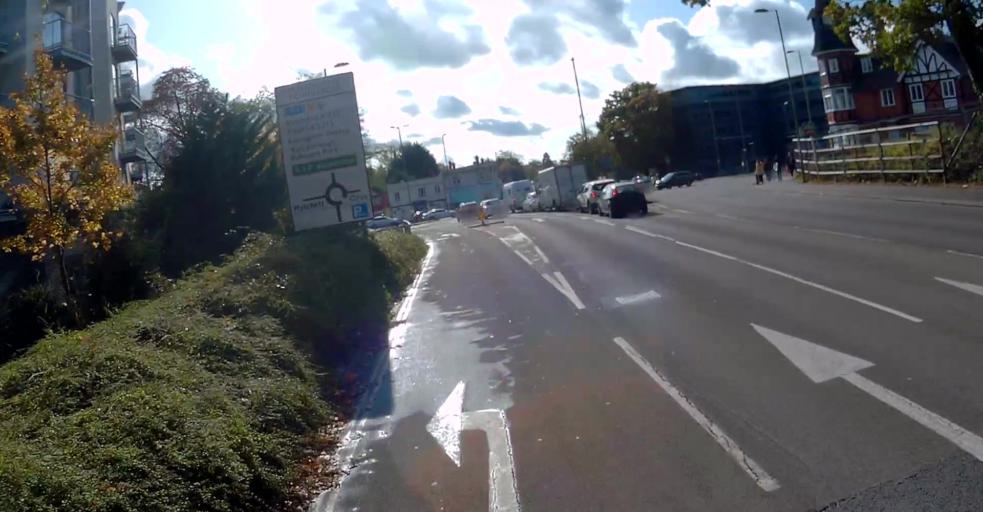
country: GB
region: England
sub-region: Hampshire
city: Farnborough
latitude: 51.2948
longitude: -0.7533
